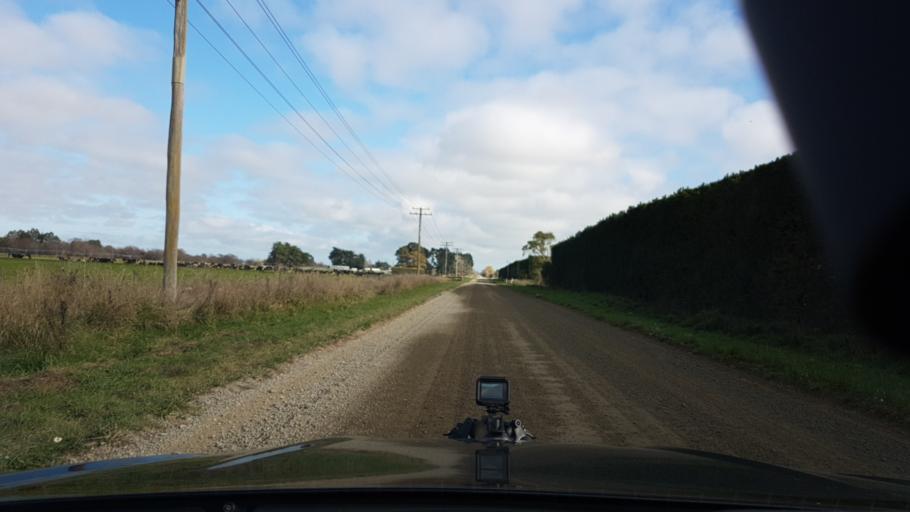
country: NZ
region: Canterbury
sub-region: Waimakariri District
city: Woodend
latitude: -43.3227
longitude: 172.6217
